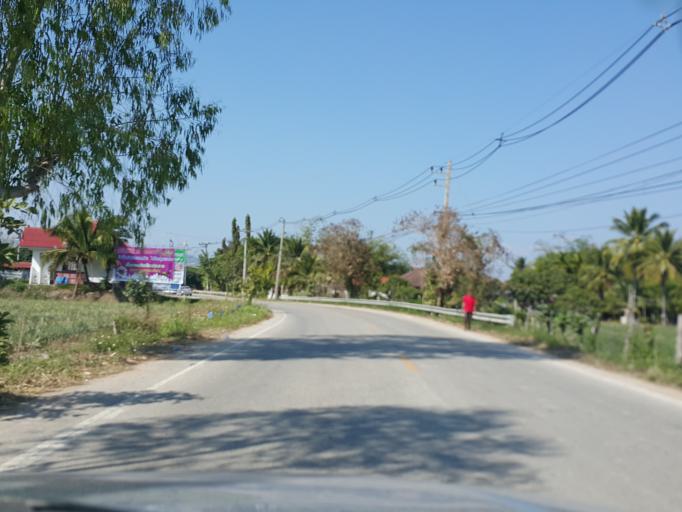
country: TH
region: Chiang Mai
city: Mae Wang
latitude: 18.6031
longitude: 98.7989
